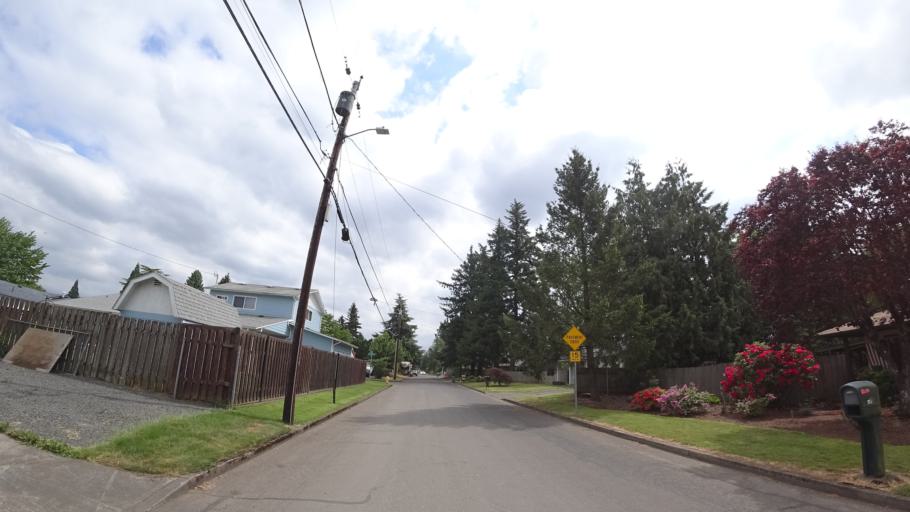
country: US
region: Oregon
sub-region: Multnomah County
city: Gresham
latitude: 45.5104
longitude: -122.4808
